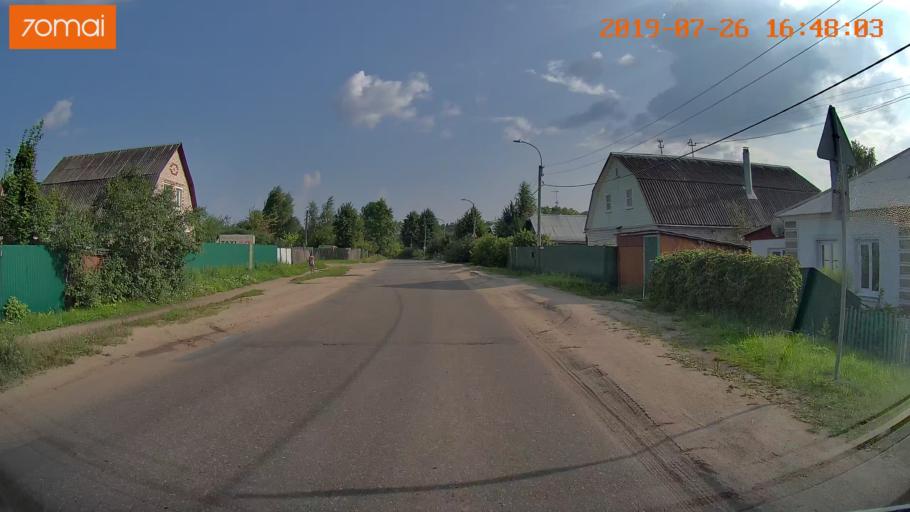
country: RU
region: Ivanovo
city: Bogorodskoye
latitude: 57.0372
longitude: 41.0125
